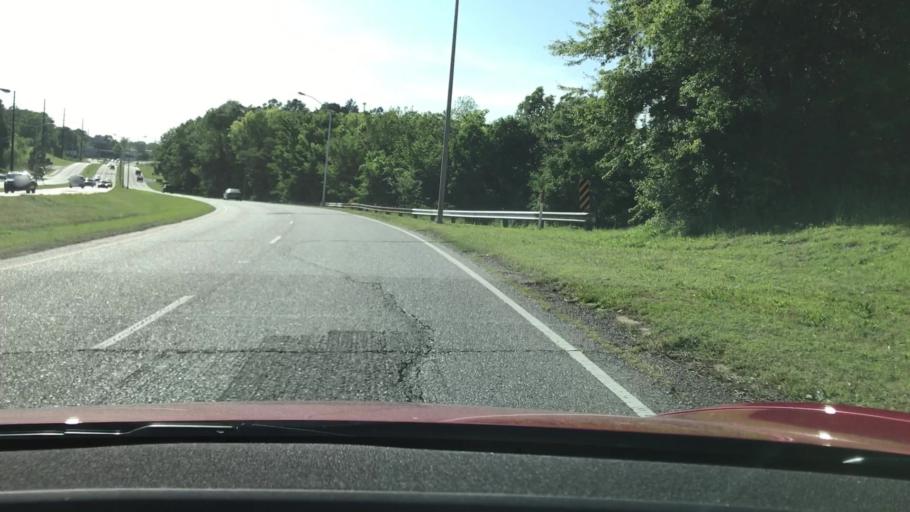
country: US
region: Louisiana
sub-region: Bossier Parish
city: Bossier City
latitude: 32.5040
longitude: -93.7272
